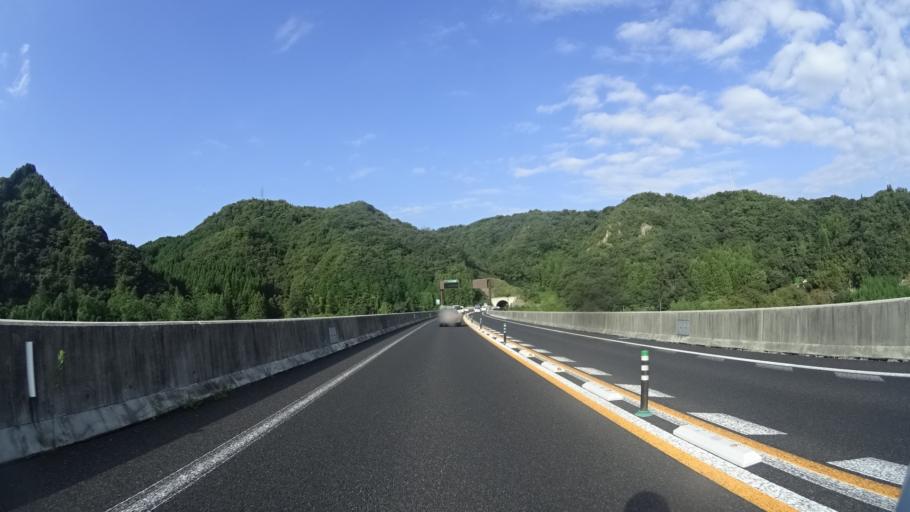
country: JP
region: Shimane
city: Izumo
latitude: 35.3240
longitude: 132.7638
